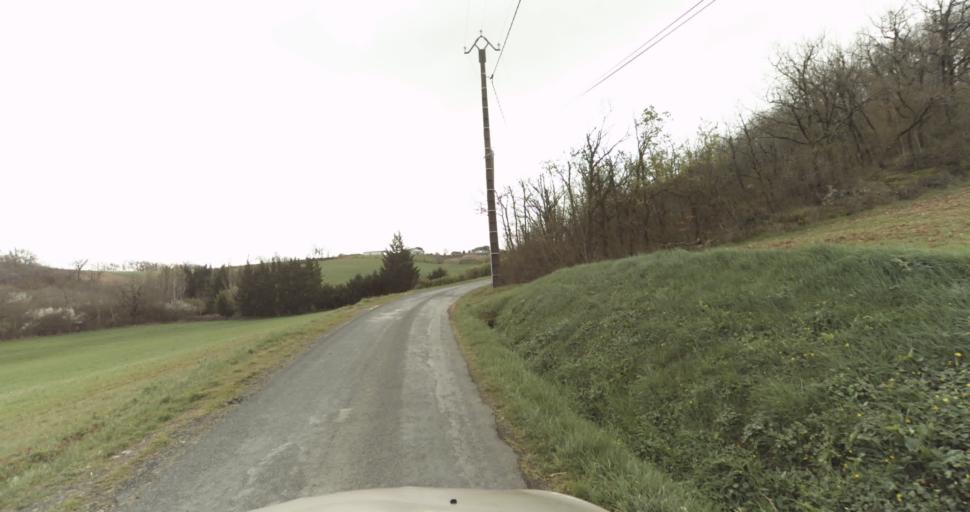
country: FR
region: Midi-Pyrenees
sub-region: Departement du Tarn
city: Puygouzon
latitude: 43.8720
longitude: 2.1866
